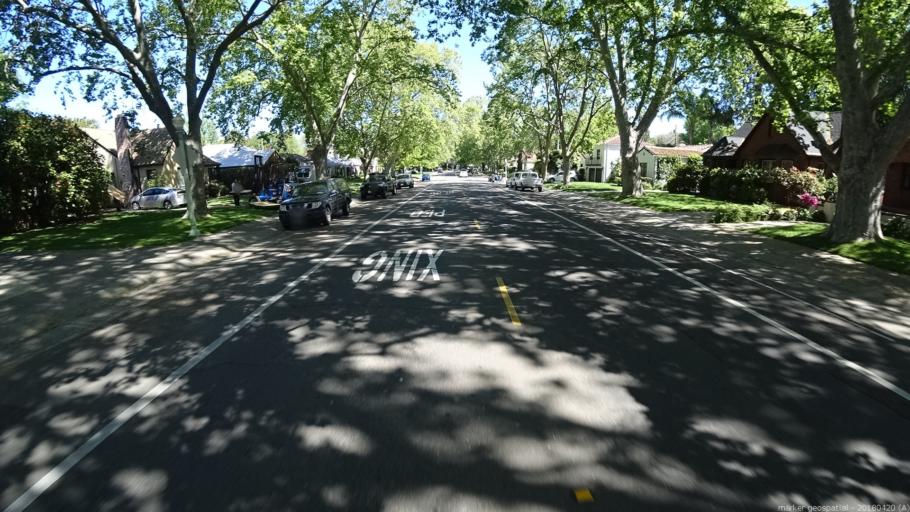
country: US
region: California
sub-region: Sacramento County
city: Sacramento
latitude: 38.5587
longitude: -121.4954
